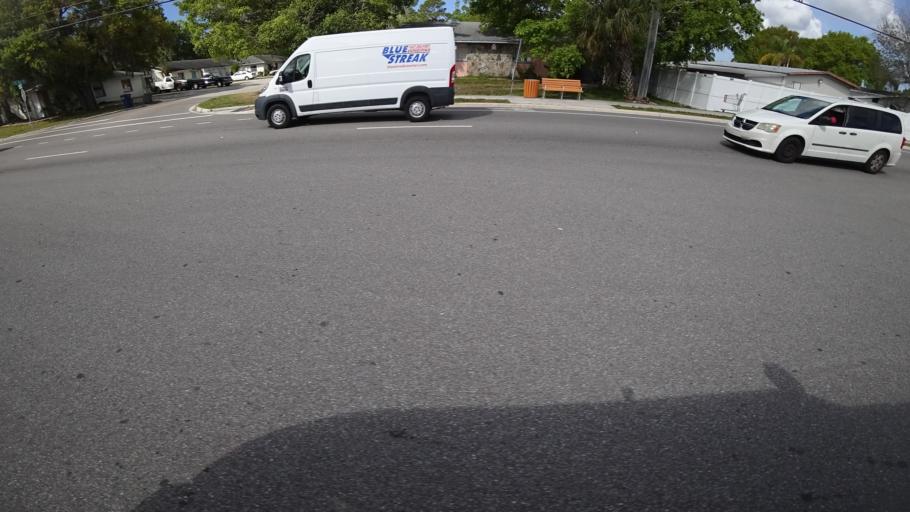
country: US
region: Florida
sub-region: Manatee County
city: West Samoset
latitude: 27.4418
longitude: -82.5548
